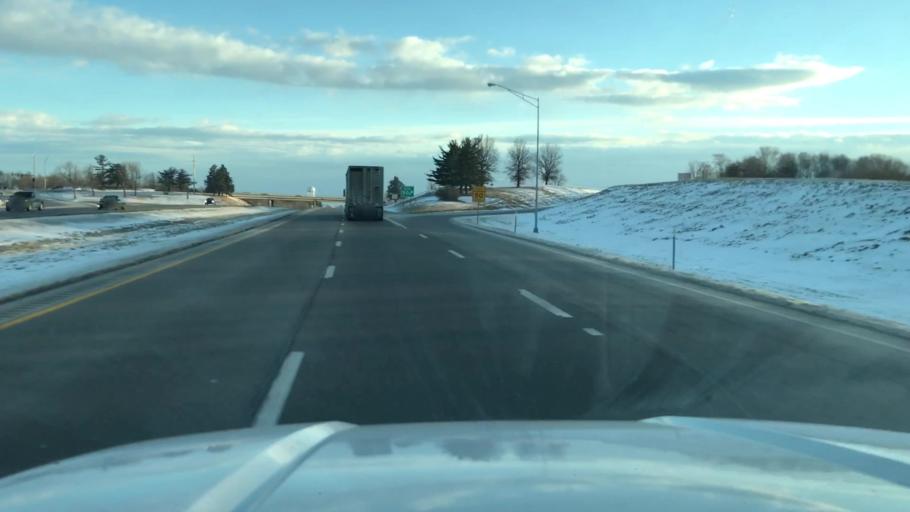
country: US
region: Missouri
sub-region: Andrew County
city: Country Club Village
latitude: 39.8187
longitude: -94.8050
